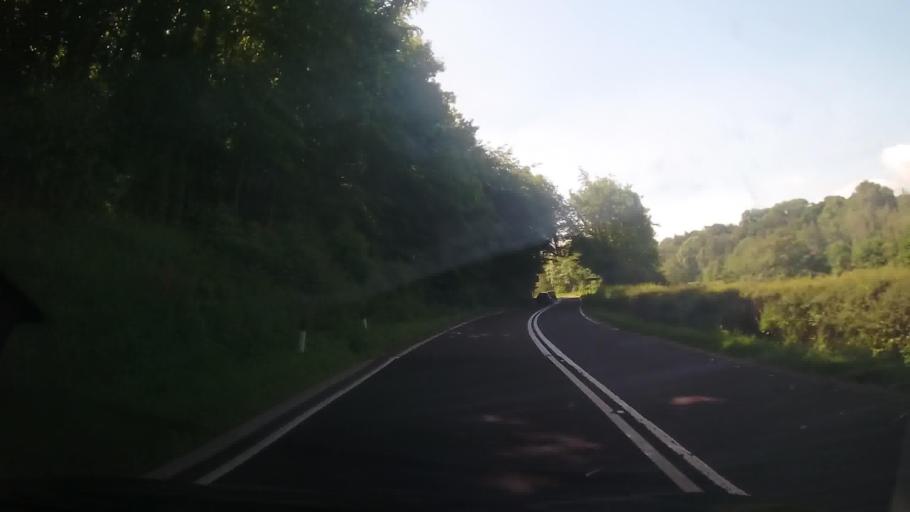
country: GB
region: England
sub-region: Shropshire
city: Church Stretton
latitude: 52.5007
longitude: -2.8188
